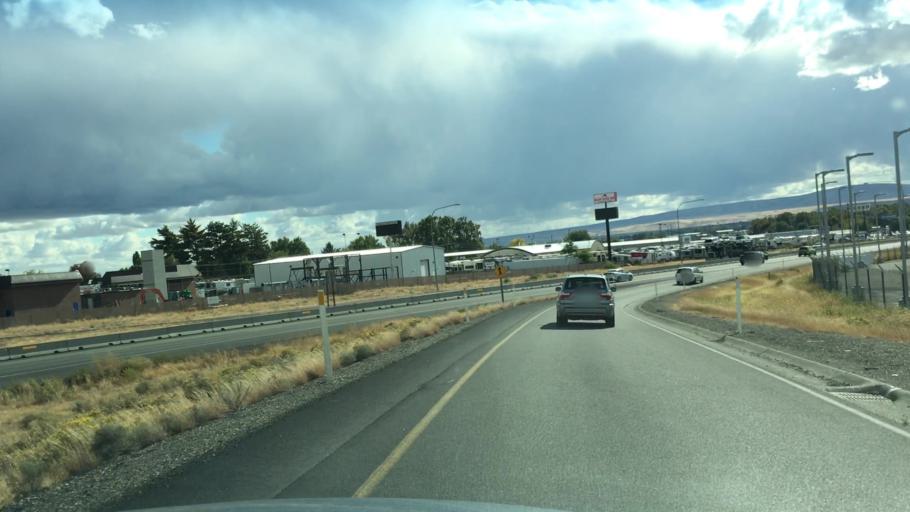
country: US
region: Washington
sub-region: Franklin County
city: Pasco
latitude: 46.2407
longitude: -119.1299
